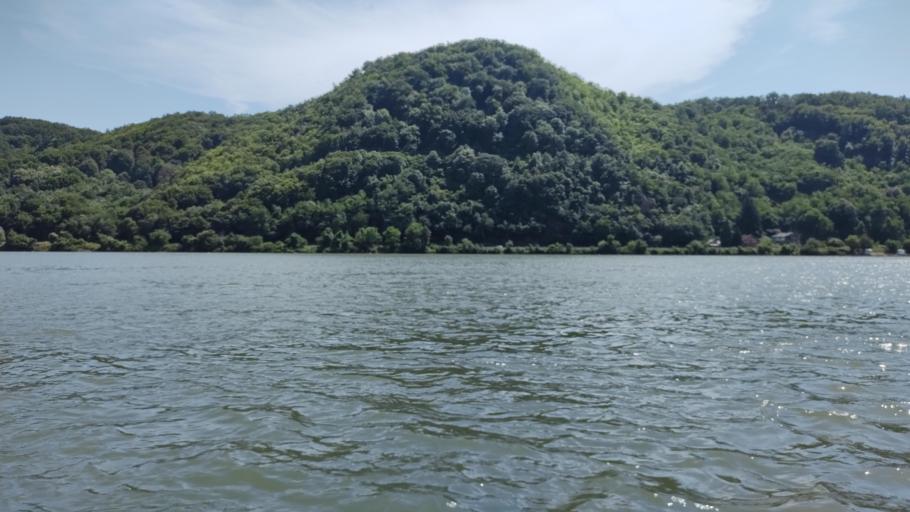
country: RS
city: Radenka
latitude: 44.6605
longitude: 21.7744
